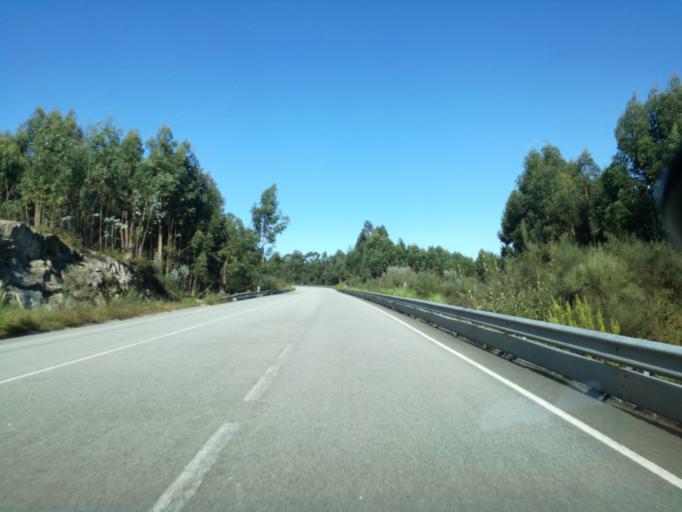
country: PT
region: Porto
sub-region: Pacos de Ferreira
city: Seroa
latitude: 41.2753
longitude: -8.4263
